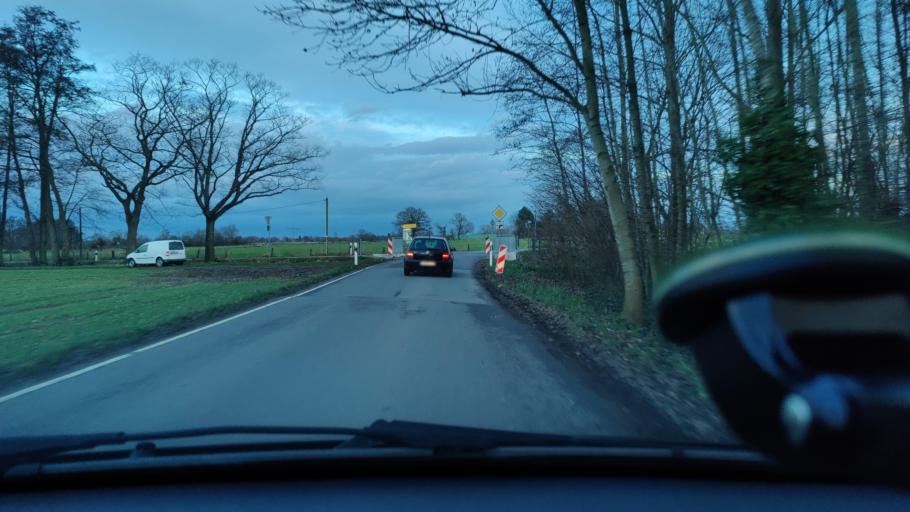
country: DE
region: North Rhine-Westphalia
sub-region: Regierungsbezirk Dusseldorf
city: Xanten
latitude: 51.6637
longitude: 6.4057
